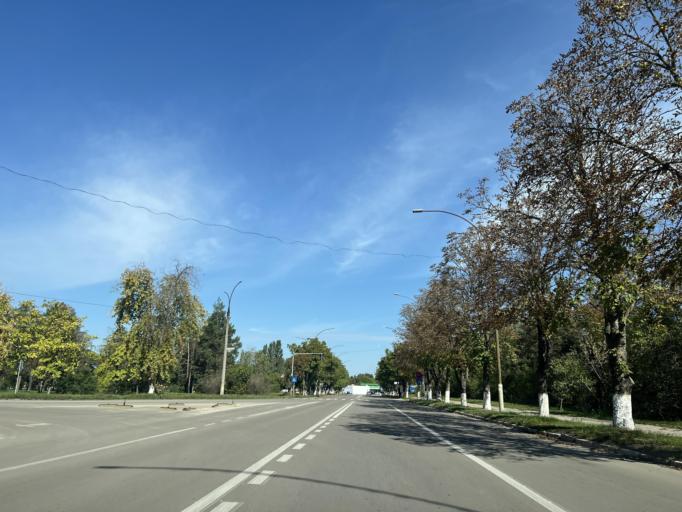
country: MD
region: Ungheni
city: Ungheni
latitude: 47.2185
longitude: 27.8089
